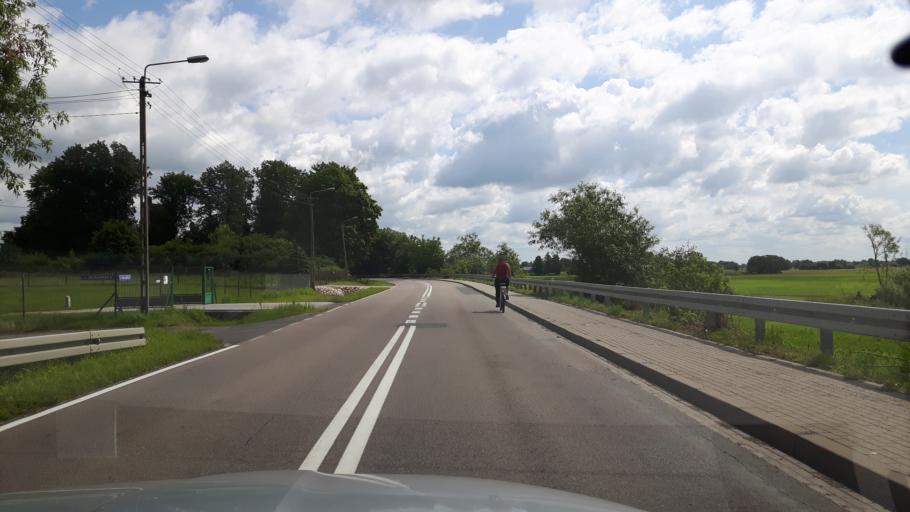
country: PL
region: Masovian Voivodeship
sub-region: Powiat ostrowski
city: Brok
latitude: 52.7004
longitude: 21.8716
